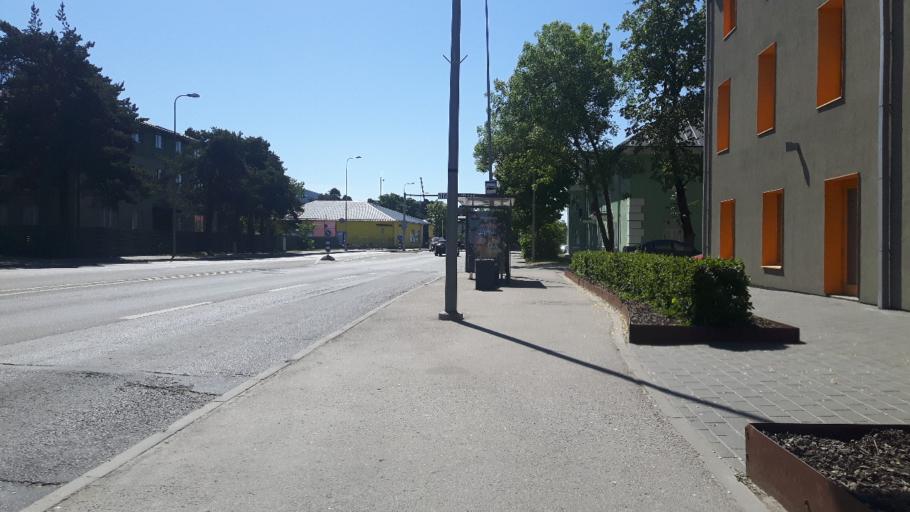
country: EE
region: Harju
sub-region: Tallinna linn
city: Tallinn
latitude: 59.3747
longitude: 24.7178
